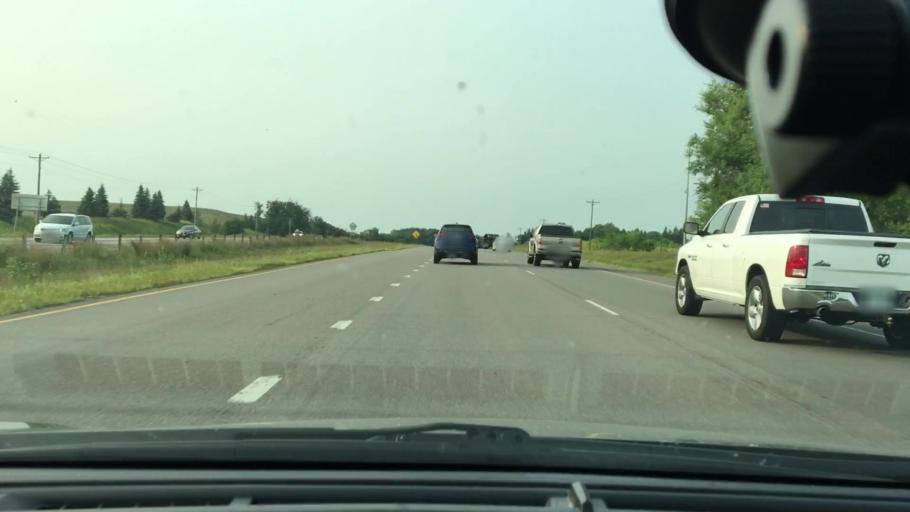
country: US
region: Minnesota
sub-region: Sherburne County
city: Elk River
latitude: 45.3745
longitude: -93.5629
